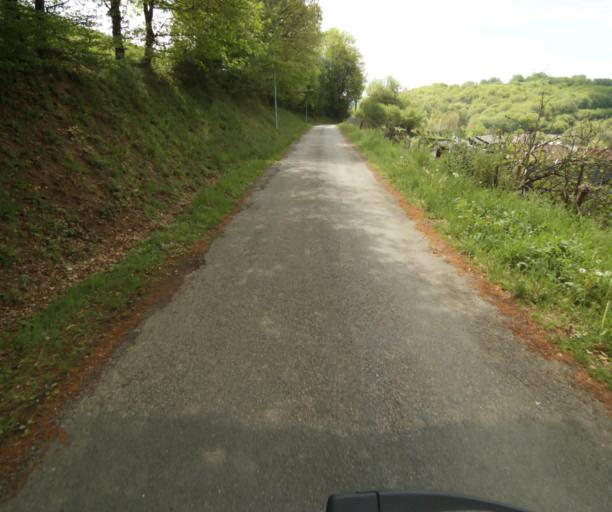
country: FR
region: Limousin
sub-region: Departement de la Correze
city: Tulle
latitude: 45.2899
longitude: 1.7658
